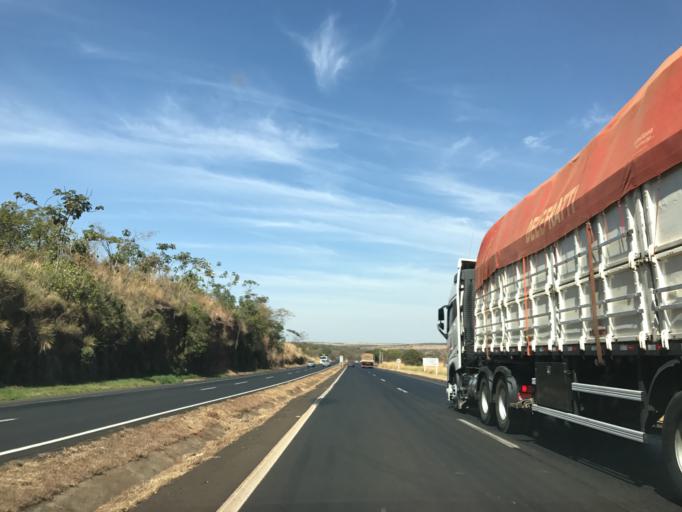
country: BR
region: Minas Gerais
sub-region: Monte Alegre De Minas
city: Monte Alegre de Minas
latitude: -18.7813
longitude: -49.0796
